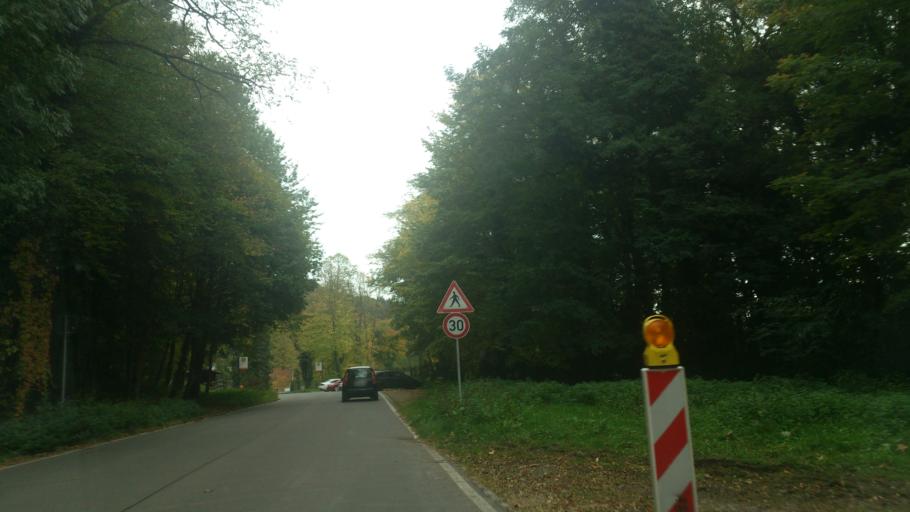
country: DE
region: Baden-Wuerttemberg
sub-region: Karlsruhe Region
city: Heidelberg
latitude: 49.3895
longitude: 8.7065
